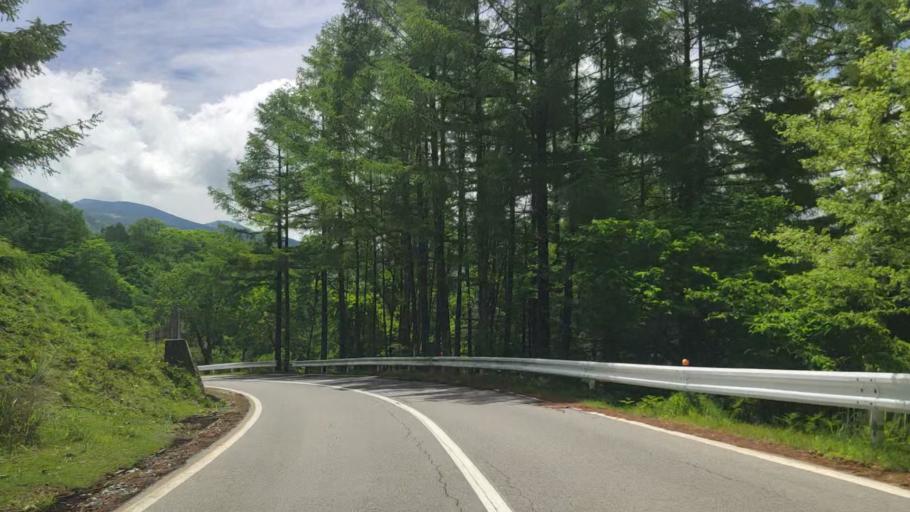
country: JP
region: Nagano
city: Chino
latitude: 36.0827
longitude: 138.2831
